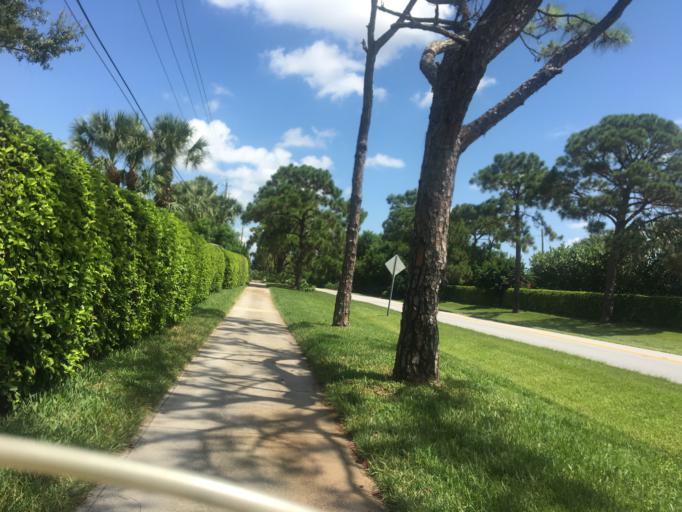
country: US
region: Florida
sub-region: Martin County
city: Palm City
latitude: 27.1518
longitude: -80.2699
